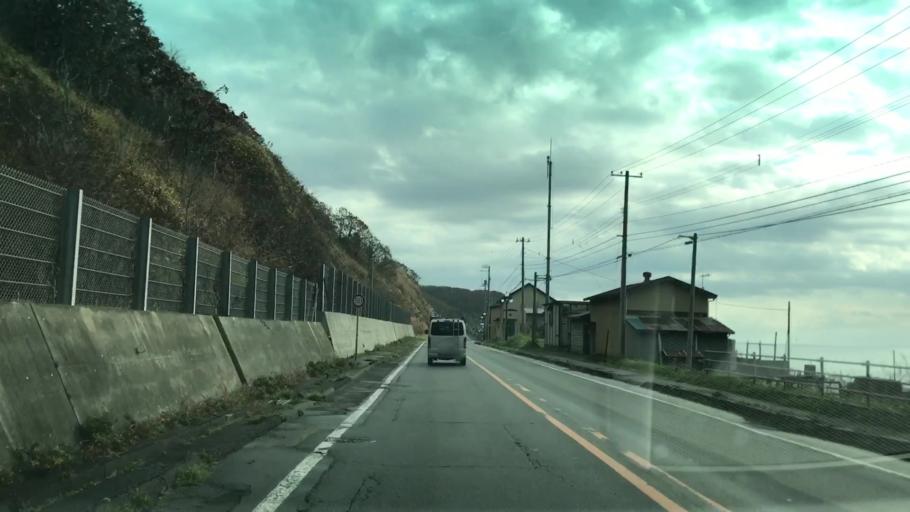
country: JP
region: Hokkaido
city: Shizunai-furukawacho
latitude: 42.1534
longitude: 142.7953
